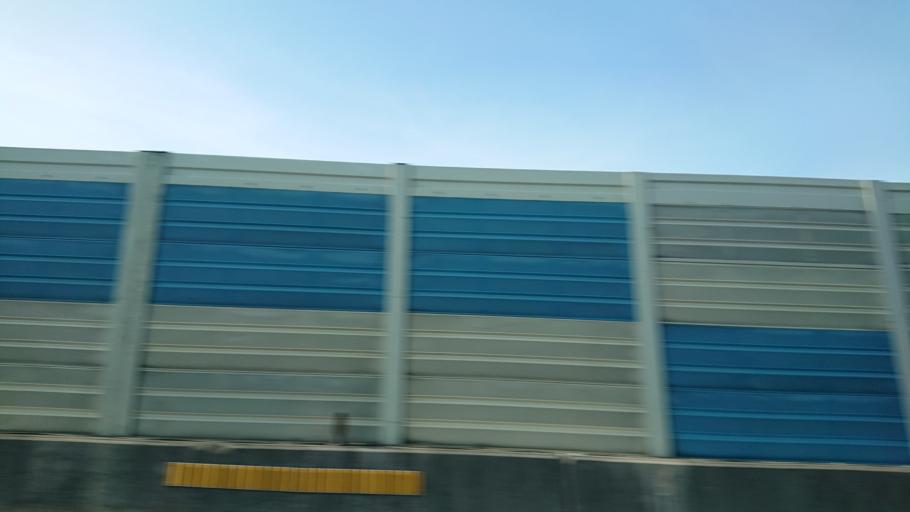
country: TW
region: Taiwan
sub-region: Taichung City
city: Taichung
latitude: 24.1972
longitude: 120.6437
